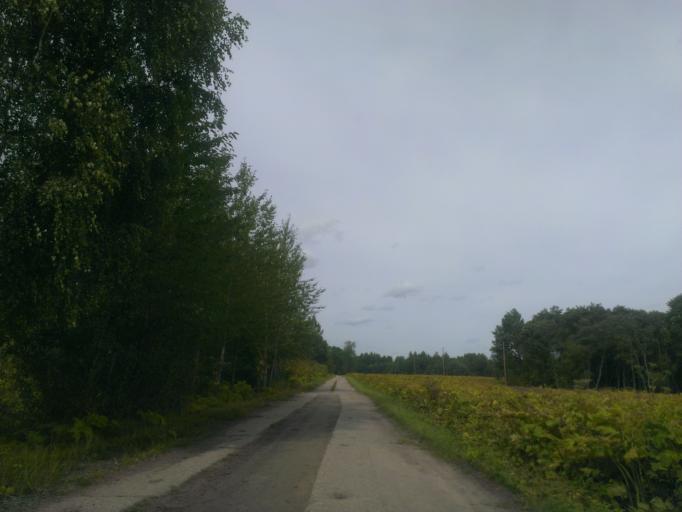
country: LV
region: Ligatne
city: Ligatne
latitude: 57.2264
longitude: 24.9564
